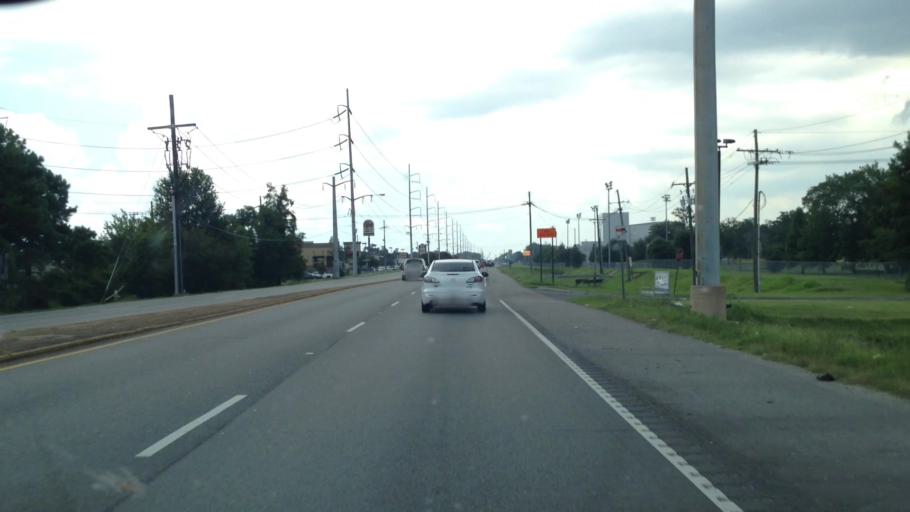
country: US
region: Louisiana
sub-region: Jefferson Parish
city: River Ridge
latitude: 29.9777
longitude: -90.2098
